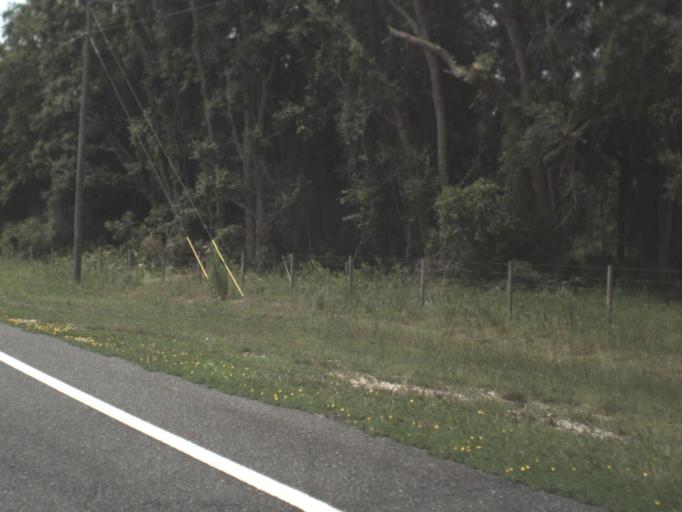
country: US
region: Florida
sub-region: Levy County
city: Chiefland
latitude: 29.4184
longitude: -82.8244
